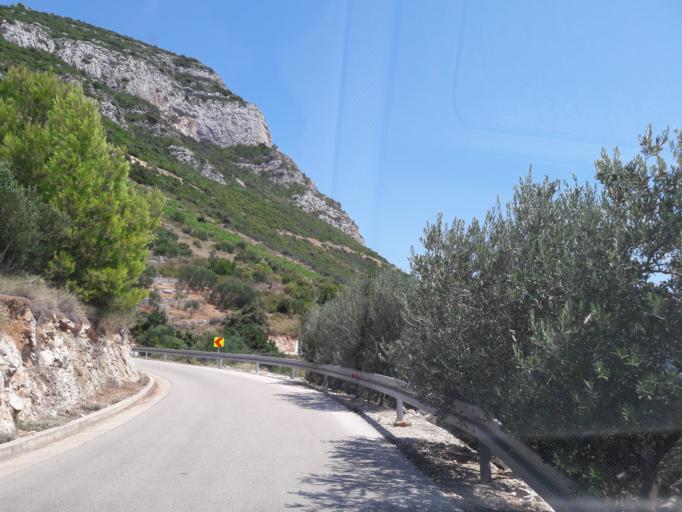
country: HR
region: Dubrovacko-Neretvanska
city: Blato
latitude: 42.9030
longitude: 17.4302
